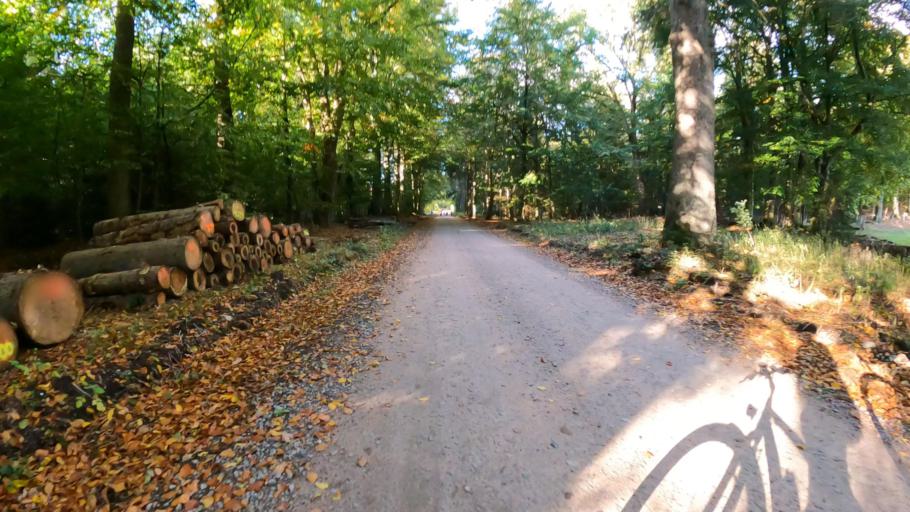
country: DE
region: Schleswig-Holstein
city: Heidmuhlen
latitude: 53.9565
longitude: 10.1246
